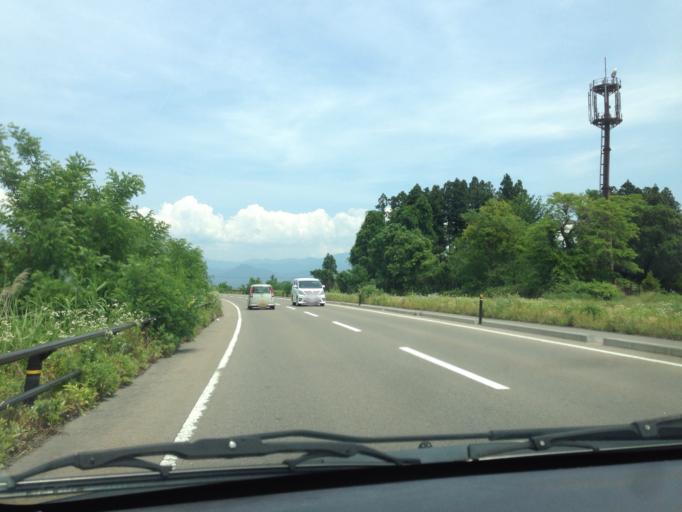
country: JP
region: Fukushima
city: Kitakata
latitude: 37.6049
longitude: 139.8469
